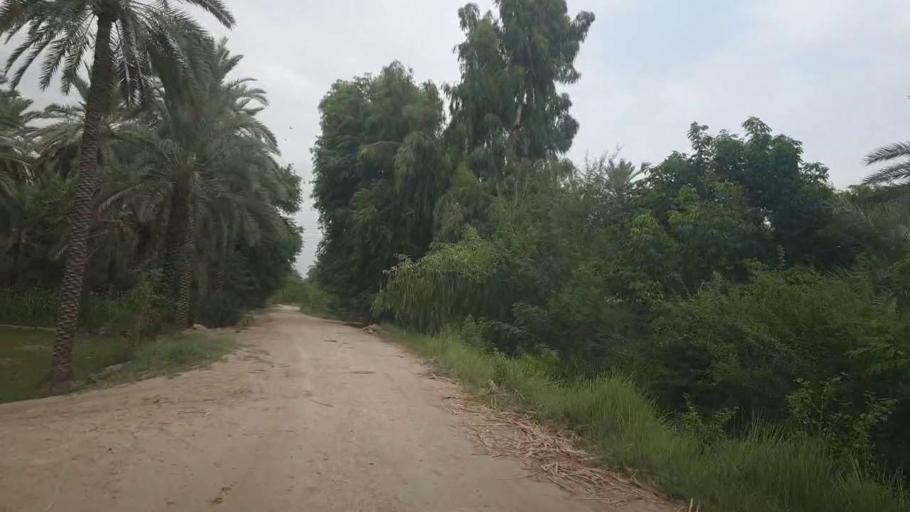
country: PK
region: Sindh
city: Khairpur
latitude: 27.5894
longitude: 68.7166
